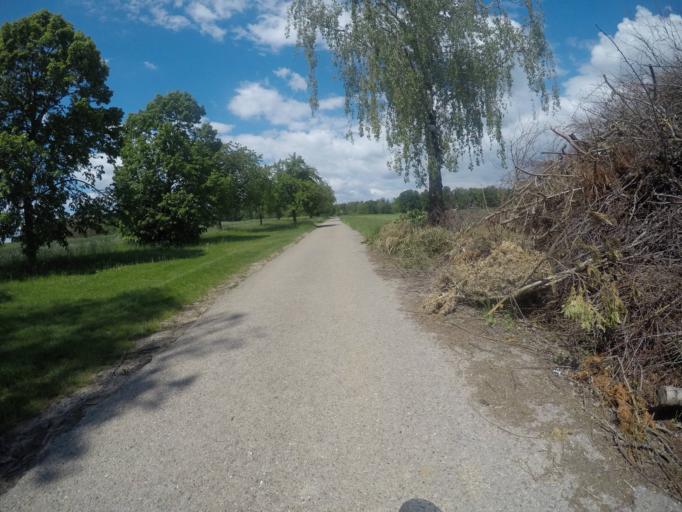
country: DE
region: Baden-Wuerttemberg
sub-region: Regierungsbezirk Stuttgart
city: Unterjettingen
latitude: 48.5844
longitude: 8.8204
